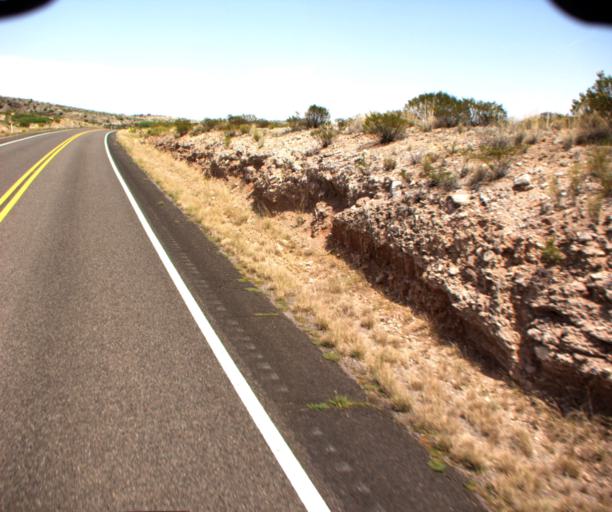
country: US
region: Arizona
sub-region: Greenlee County
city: Clifton
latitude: 32.7781
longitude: -109.3020
